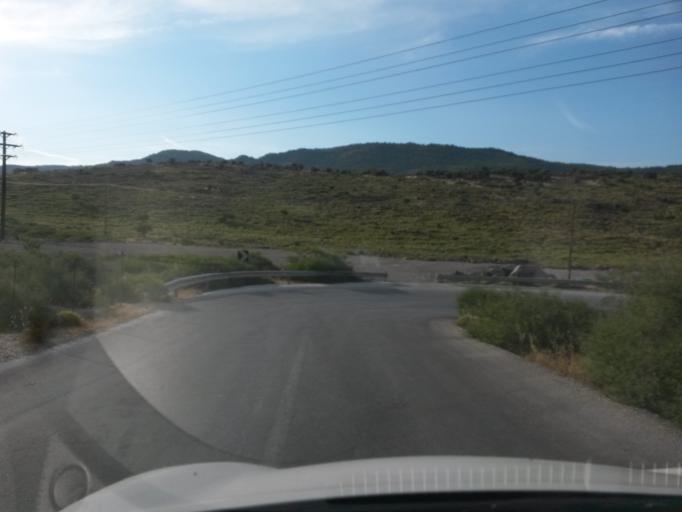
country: GR
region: North Aegean
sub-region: Nomos Lesvou
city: Kalloni
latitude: 39.2453
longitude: 26.1874
